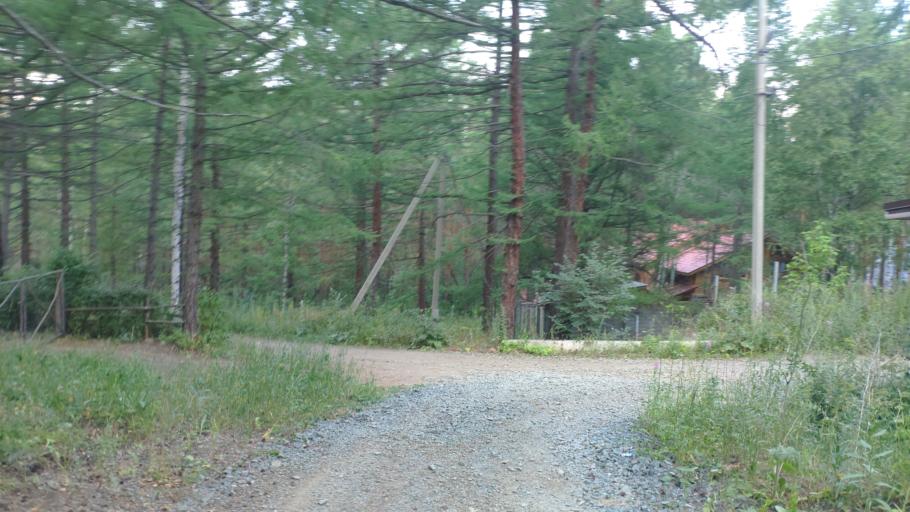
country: RU
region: Bashkortostan
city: Abzakovo
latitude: 53.8047
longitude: 58.6432
